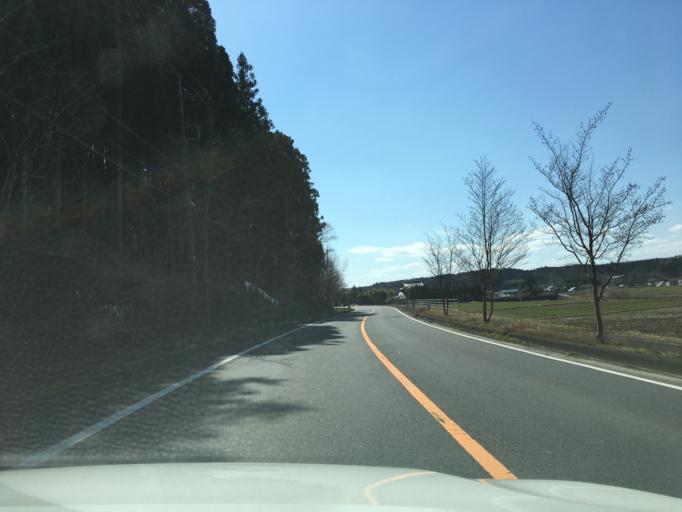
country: JP
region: Tochigi
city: Kuroiso
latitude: 36.9470
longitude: 140.1471
